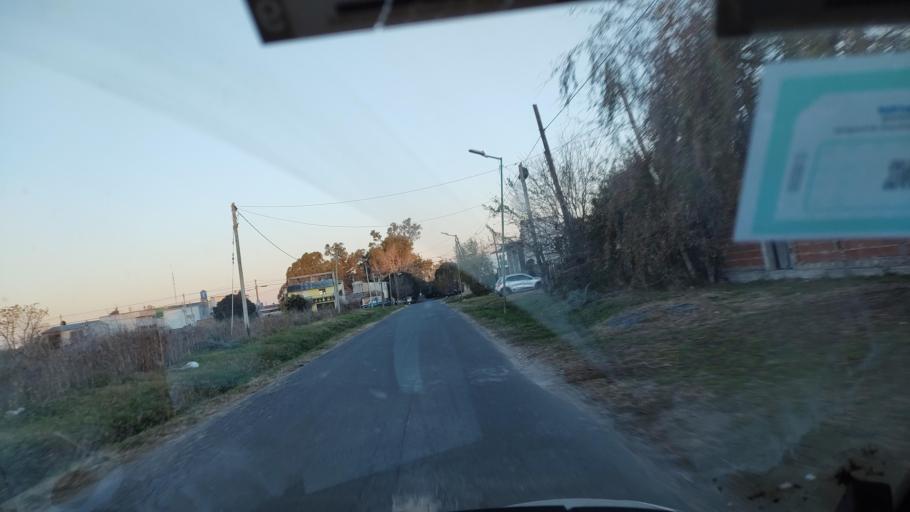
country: AR
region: Buenos Aires
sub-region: Partido de La Plata
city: La Plata
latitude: -34.9098
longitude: -58.0176
